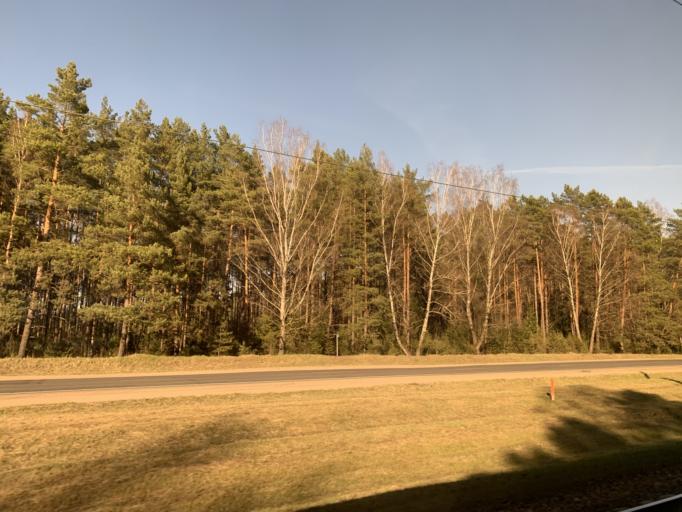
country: BY
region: Grodnenskaya
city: Smarhon'
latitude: 54.4435
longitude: 26.4969
